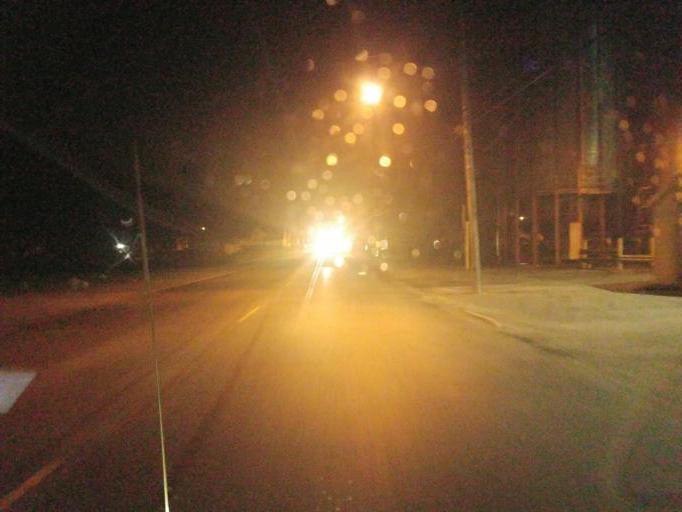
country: US
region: Ohio
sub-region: Williams County
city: Bryan
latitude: 41.3818
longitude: -84.5260
